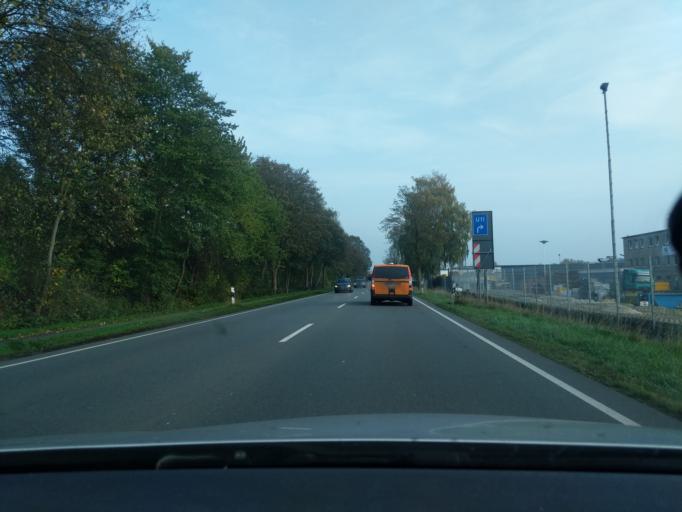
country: DE
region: Lower Saxony
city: Stade
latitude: 53.5824
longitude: 9.4898
